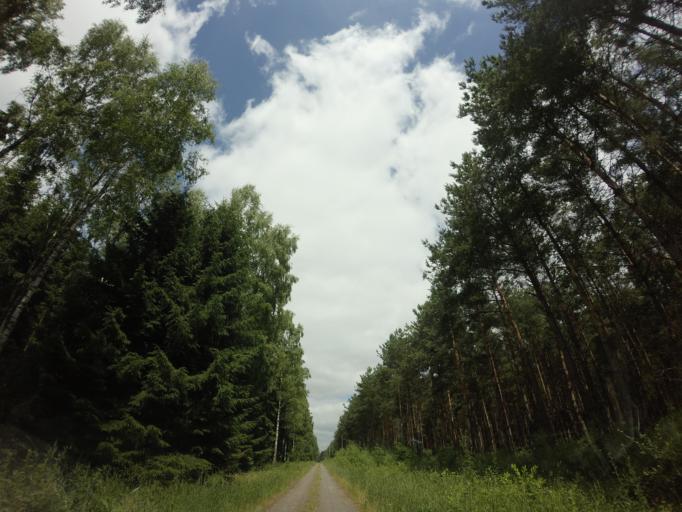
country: PL
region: West Pomeranian Voivodeship
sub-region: Powiat choszczenski
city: Krzecin
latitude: 52.9889
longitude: 15.4819
